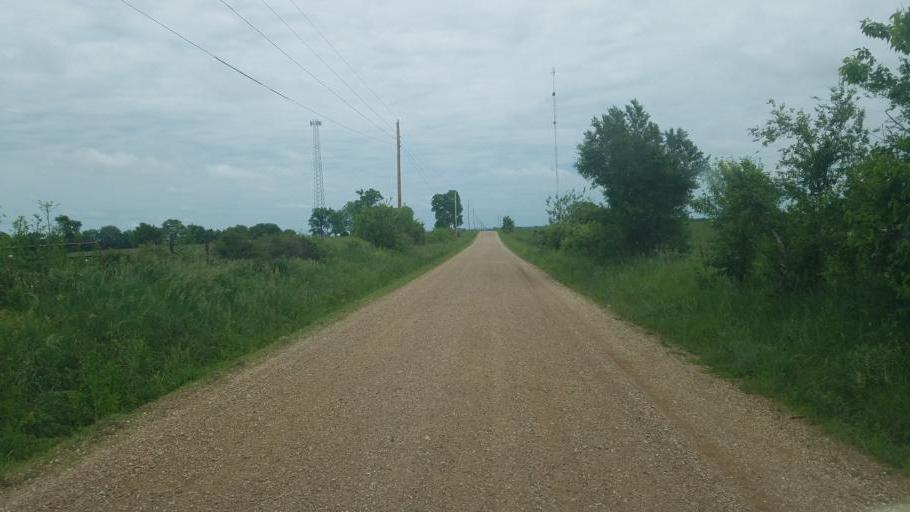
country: US
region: Missouri
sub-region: Morgan County
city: Versailles
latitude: 38.4930
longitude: -92.8064
